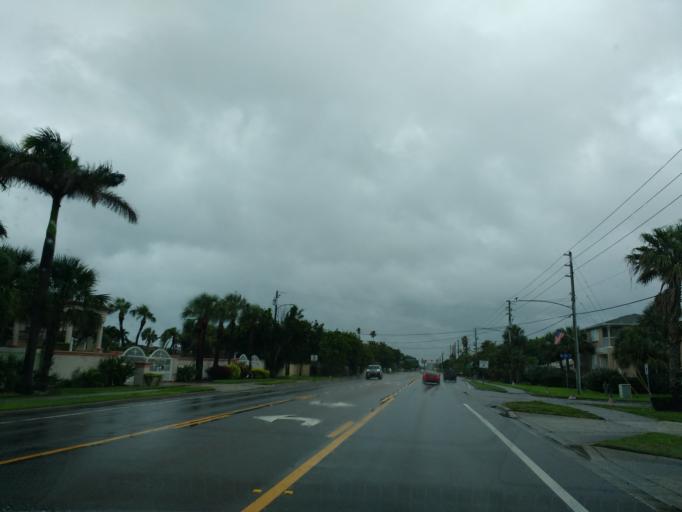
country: US
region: Florida
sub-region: Pinellas County
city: Belleair Beach
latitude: 27.9153
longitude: -82.8451
